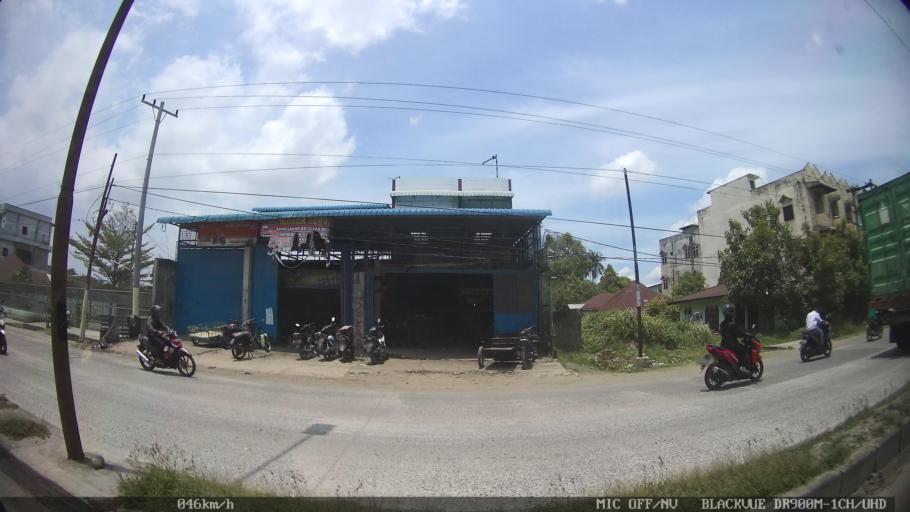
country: ID
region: North Sumatra
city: Labuhan Deli
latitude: 3.7187
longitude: 98.6805
